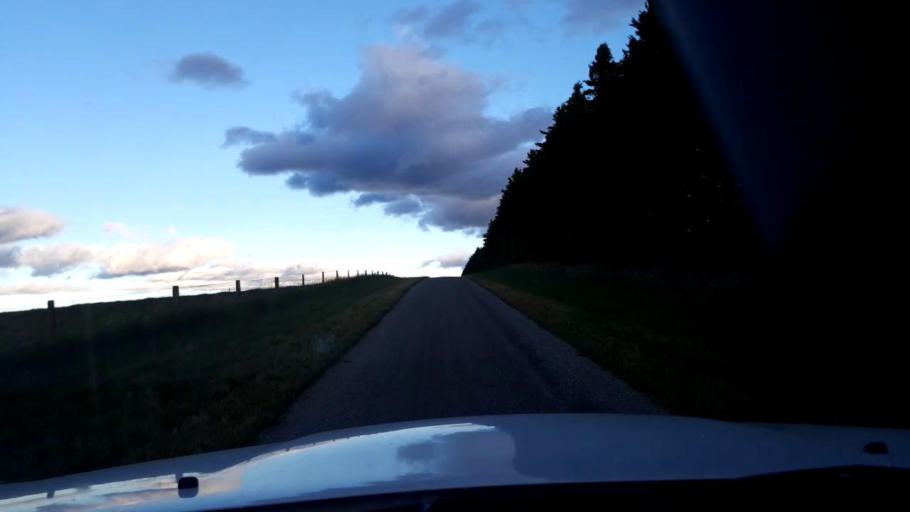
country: NZ
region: Canterbury
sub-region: Timaru District
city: Pleasant Point
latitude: -44.2619
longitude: 170.9178
